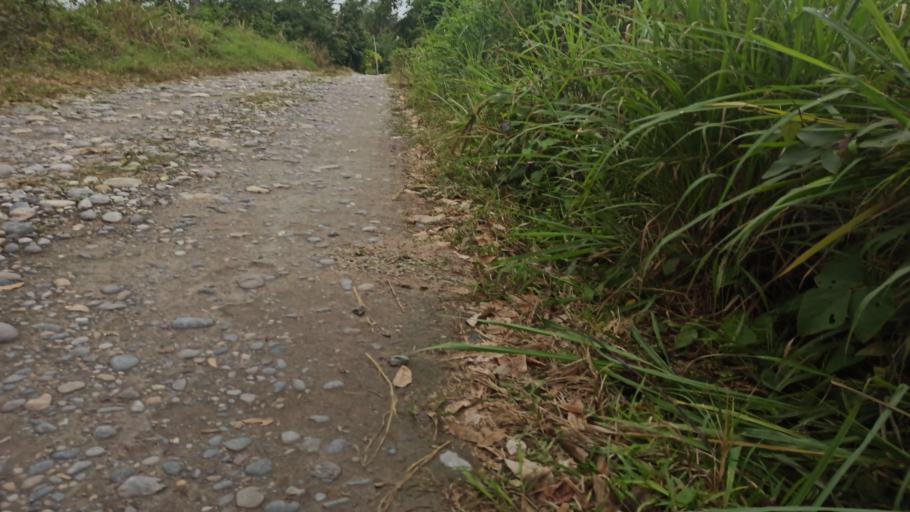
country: MX
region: Puebla
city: Espinal
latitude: 20.2918
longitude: -97.3961
